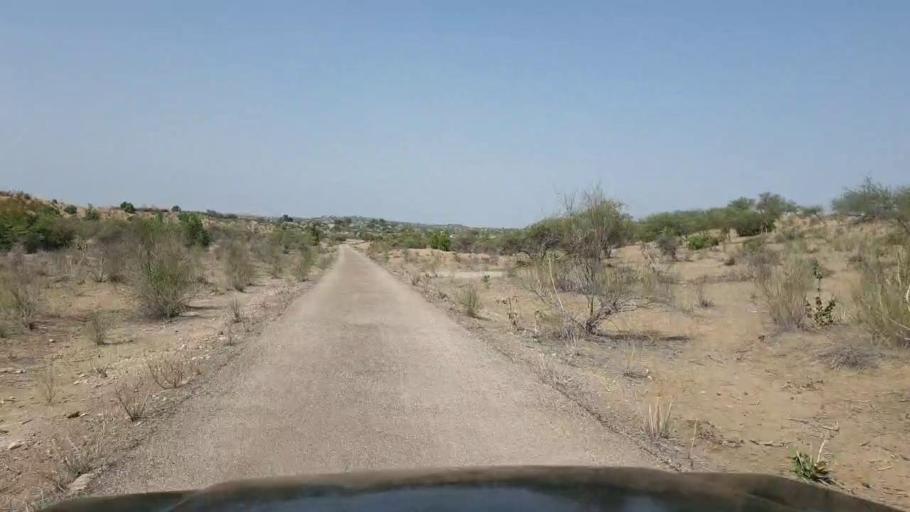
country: PK
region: Sindh
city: Mithi
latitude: 24.9650
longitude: 69.9663
